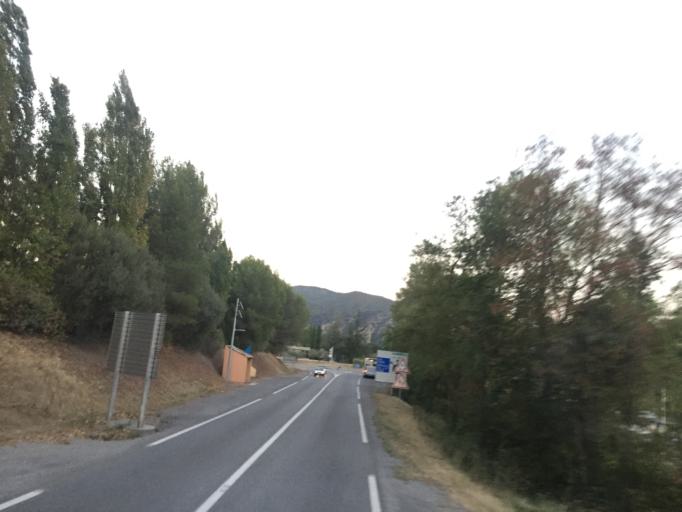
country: FR
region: Provence-Alpes-Cote d'Azur
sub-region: Departement des Alpes-de-Haute-Provence
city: Les Mees
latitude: 44.0391
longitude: 5.9604
